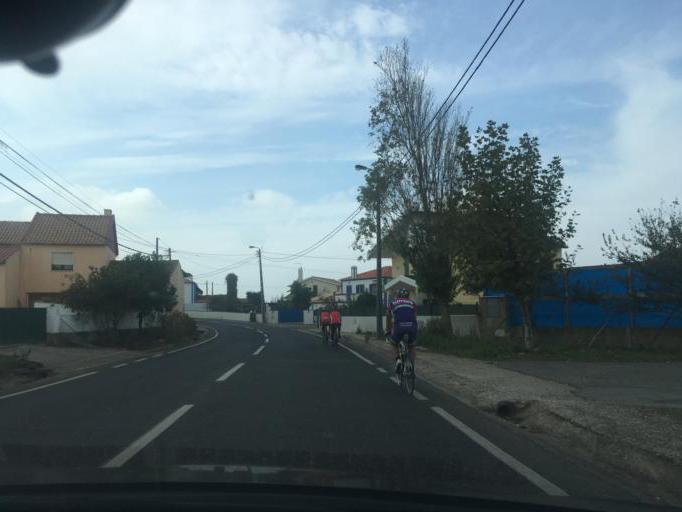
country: PT
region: Lisbon
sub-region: Sintra
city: Sao Joao das Lampas
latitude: 38.8523
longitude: -9.3964
